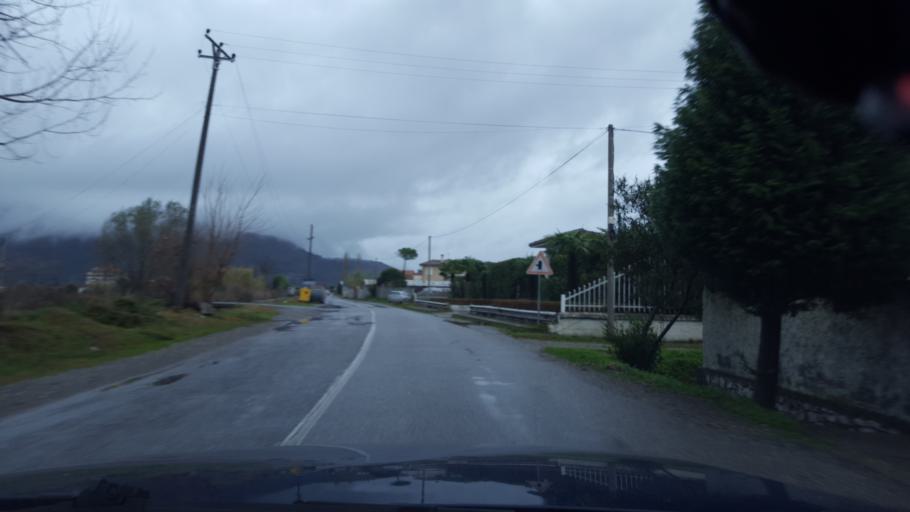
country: AL
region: Shkoder
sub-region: Rrethi i Shkodres
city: Berdica e Madhe
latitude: 42.0084
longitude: 19.4808
